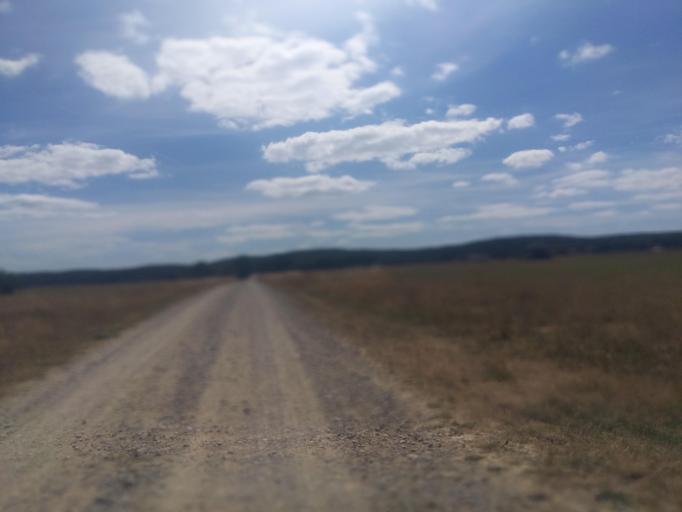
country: DE
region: Lower Saxony
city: Neu Darchau
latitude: 53.2472
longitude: 10.8524
